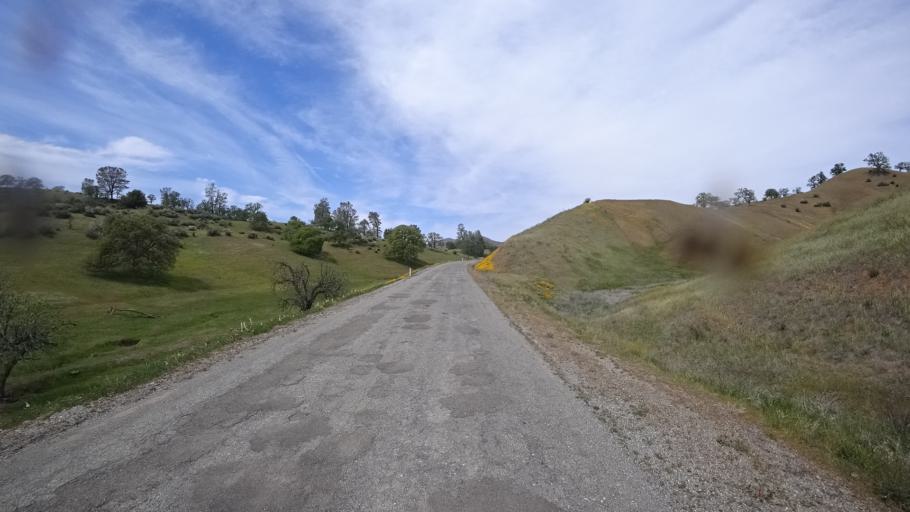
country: US
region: California
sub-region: Glenn County
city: Willows
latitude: 39.6179
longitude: -122.5918
